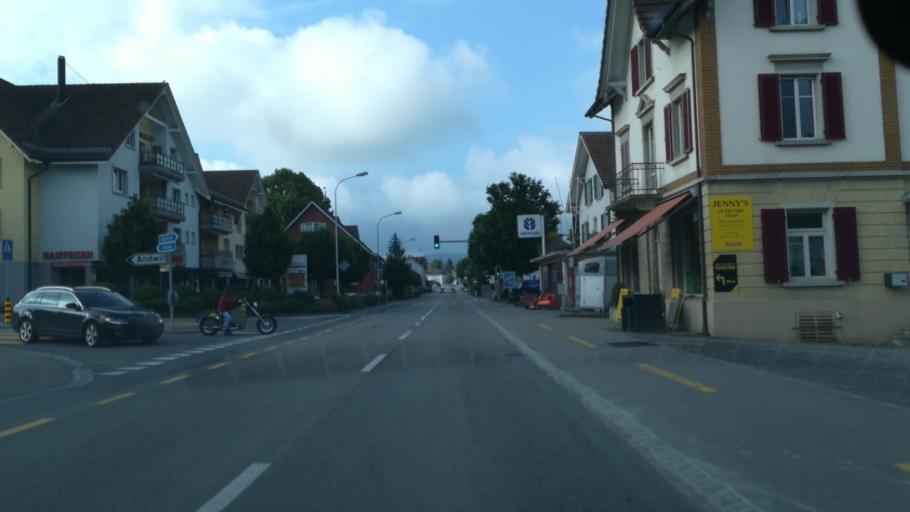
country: CH
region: Saint Gallen
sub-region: Wahlkreis St. Gallen
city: Andwil
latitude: 47.4436
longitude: 9.2556
